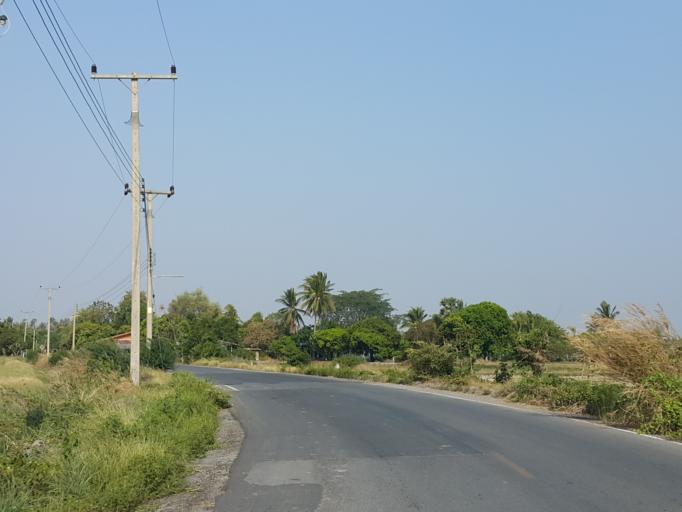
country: TH
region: Suphan Buri
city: Sam Chuk
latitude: 14.7449
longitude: 100.0356
